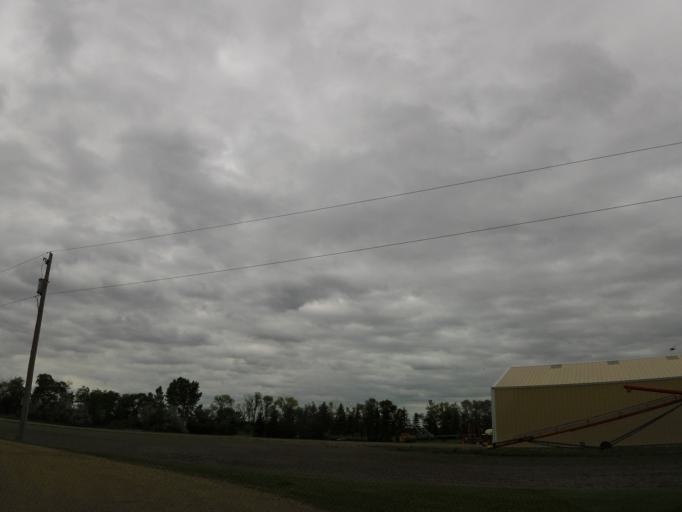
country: US
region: North Dakota
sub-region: Walsh County
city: Grafton
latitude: 48.6209
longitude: -97.4540
